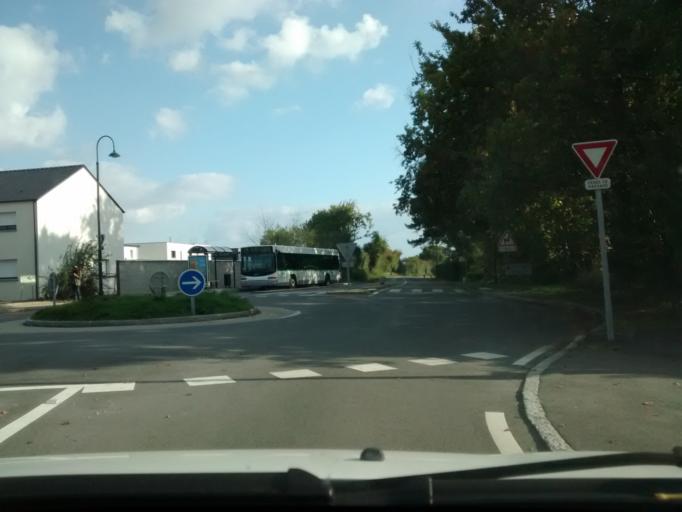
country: FR
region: Pays de la Loire
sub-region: Departement de la Loire-Atlantique
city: Orvault
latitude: 47.2790
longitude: -1.6406
